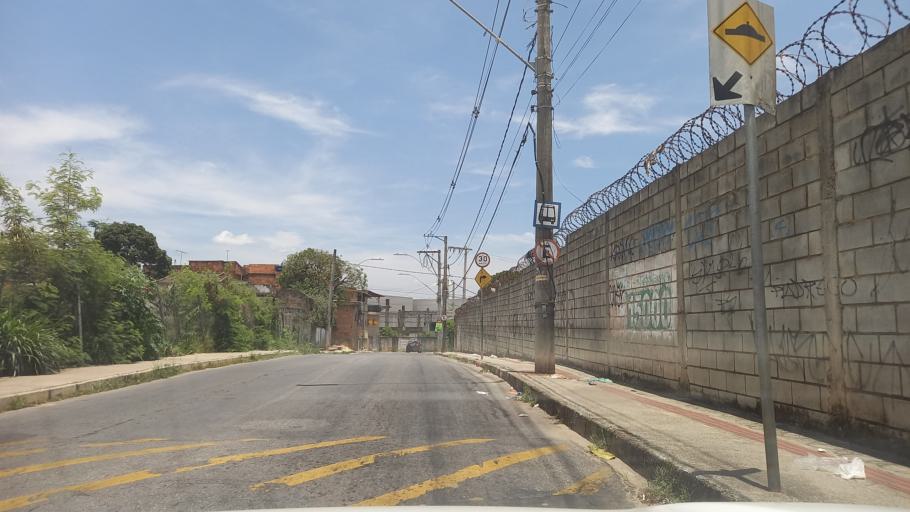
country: BR
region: Minas Gerais
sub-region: Belo Horizonte
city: Belo Horizonte
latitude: -19.8606
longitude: -43.9229
